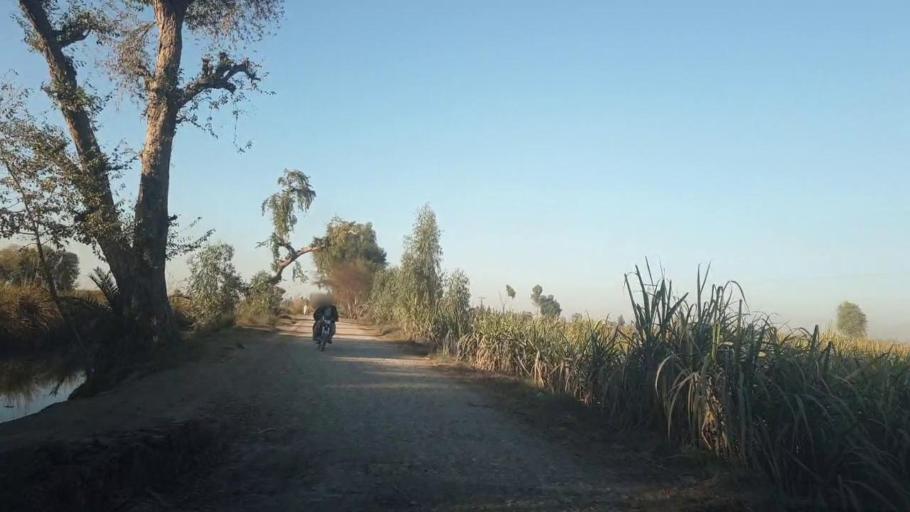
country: PK
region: Sindh
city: Ghotki
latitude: 27.9945
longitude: 69.2721
